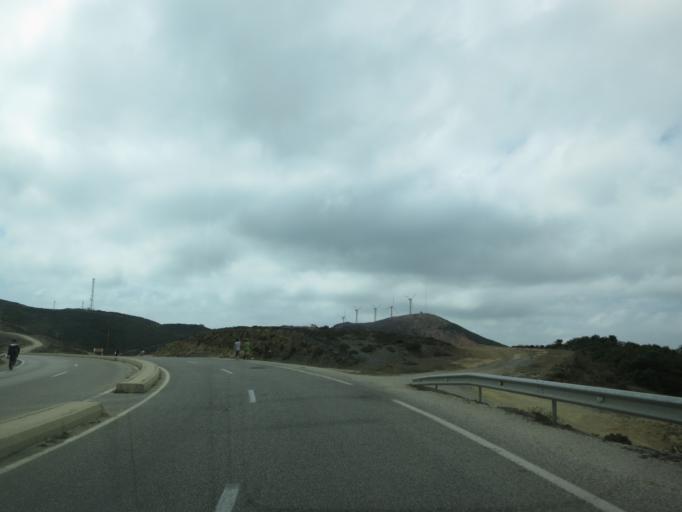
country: ES
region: Ceuta
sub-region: Ceuta
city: Ceuta
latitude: 35.8583
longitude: -5.4308
